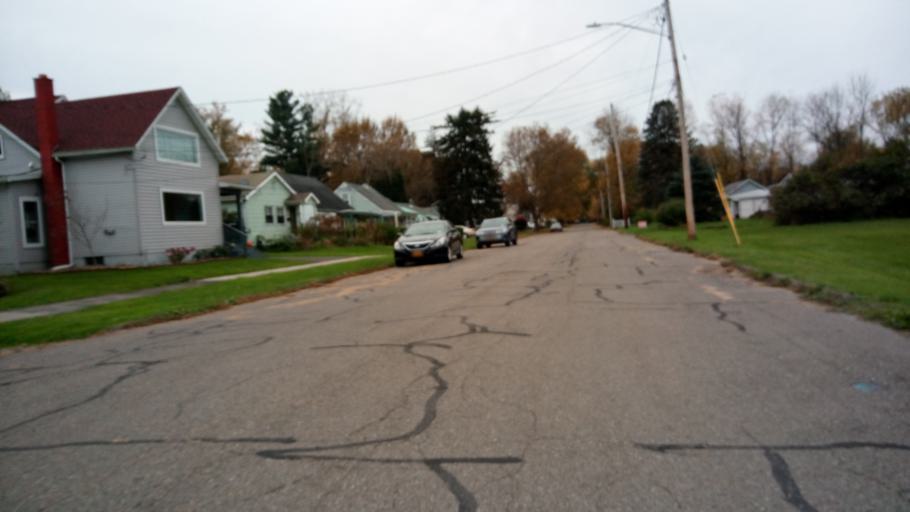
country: US
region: New York
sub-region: Chemung County
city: Elmira
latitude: 42.0831
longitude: -76.7843
